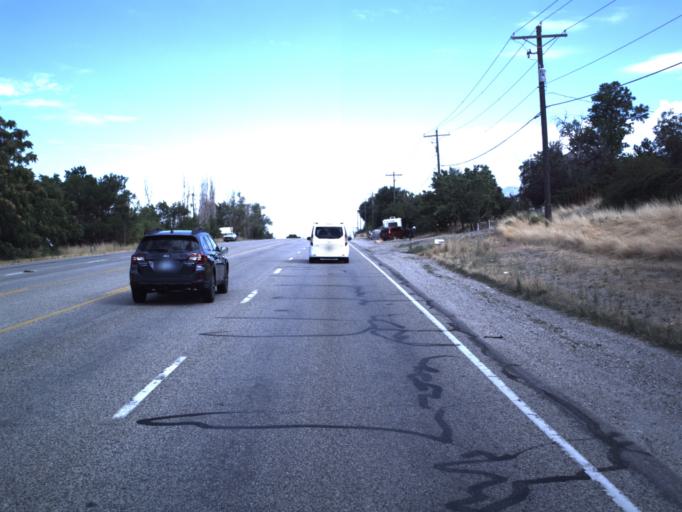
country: US
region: Utah
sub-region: Box Elder County
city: Willard
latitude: 41.4369
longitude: -112.0361
